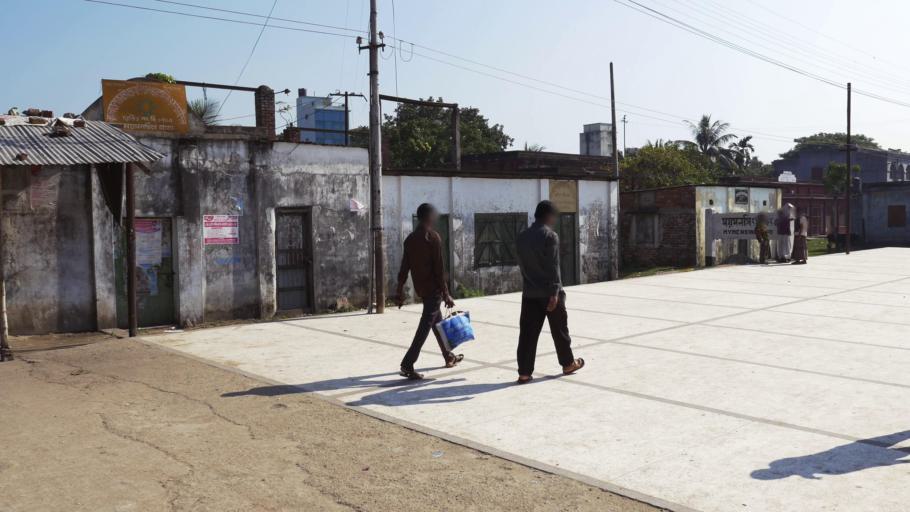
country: BD
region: Dhaka
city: Mymensingh
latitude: 24.7012
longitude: 90.4488
